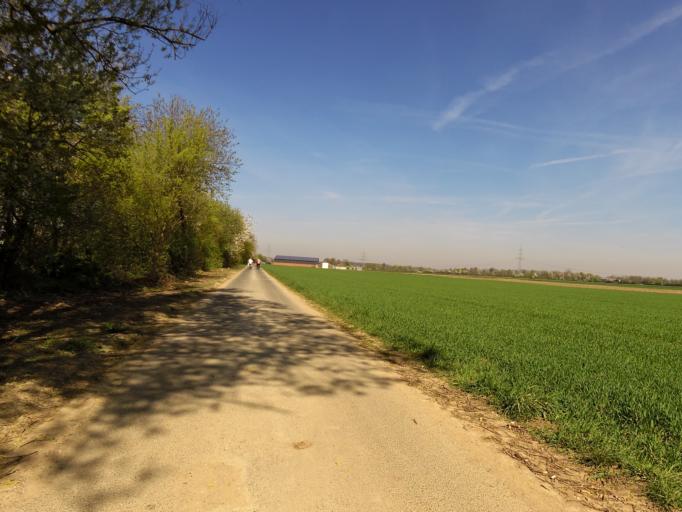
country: DE
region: North Rhine-Westphalia
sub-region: Regierungsbezirk Koln
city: Rheinbach
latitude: 50.6376
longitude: 6.9376
